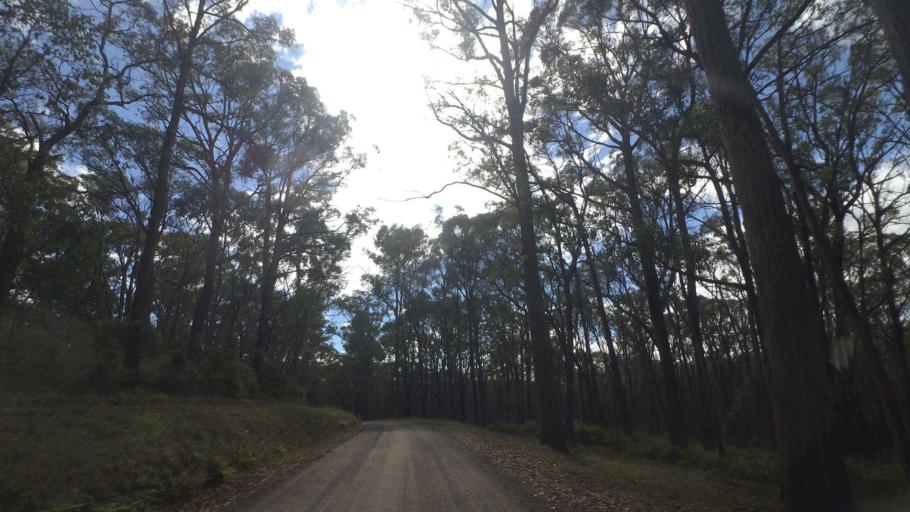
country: AU
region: Victoria
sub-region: Cardinia
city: Gembrook
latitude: -37.9044
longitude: 145.5897
